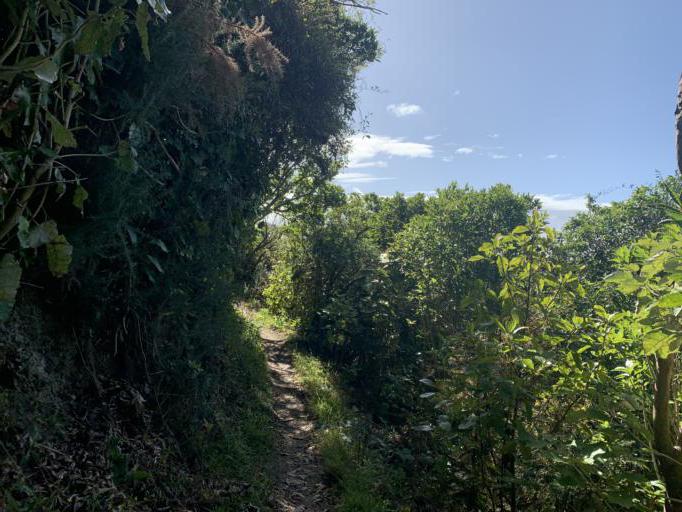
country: NZ
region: Wellington
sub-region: Wellington City
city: Brooklyn
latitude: -41.2995
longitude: 174.7543
